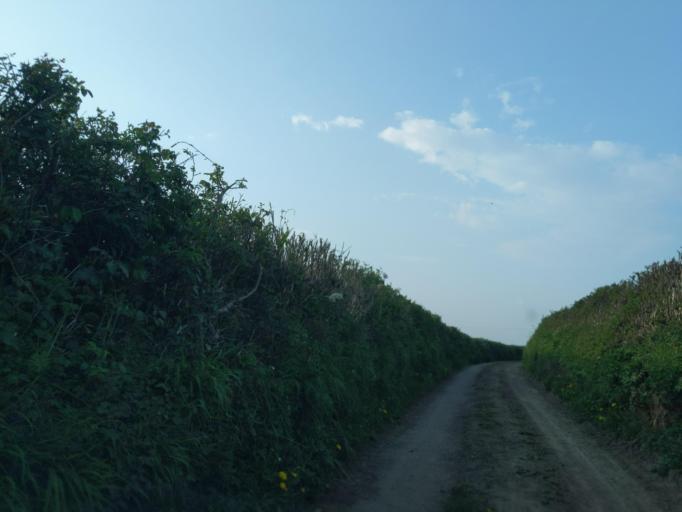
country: GB
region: England
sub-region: Devon
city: Yealmpton
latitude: 50.3557
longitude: -4.0388
